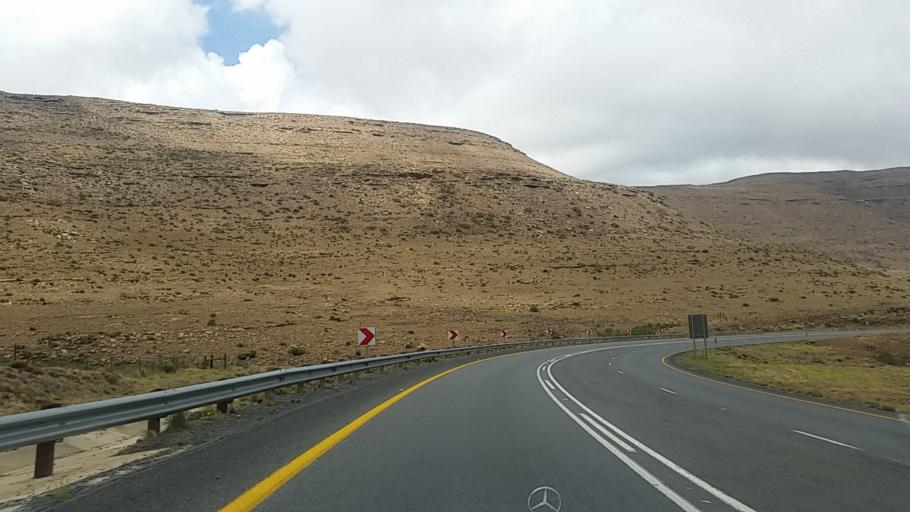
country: ZA
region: Eastern Cape
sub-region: Chris Hani District Municipality
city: Middelburg
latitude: -31.8458
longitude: 24.8801
